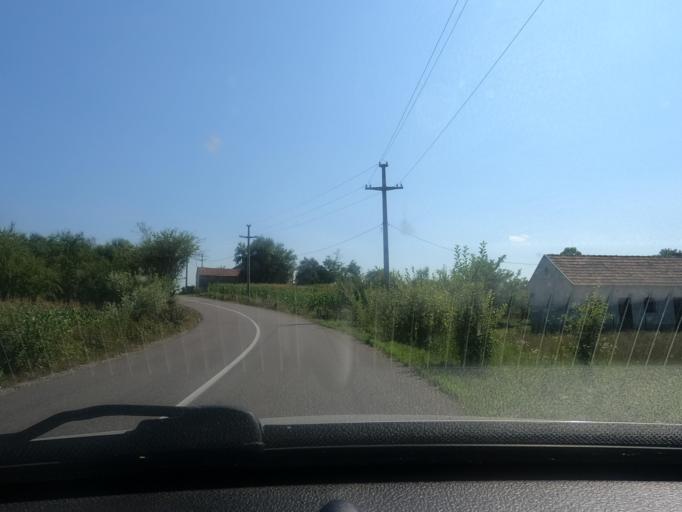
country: RS
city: Kozjak
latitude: 44.5538
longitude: 19.3134
